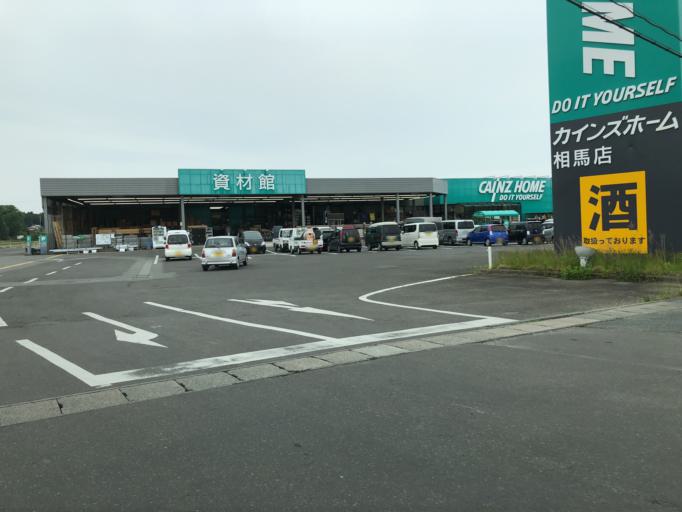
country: JP
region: Miyagi
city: Marumori
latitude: 37.7876
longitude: 140.9323
